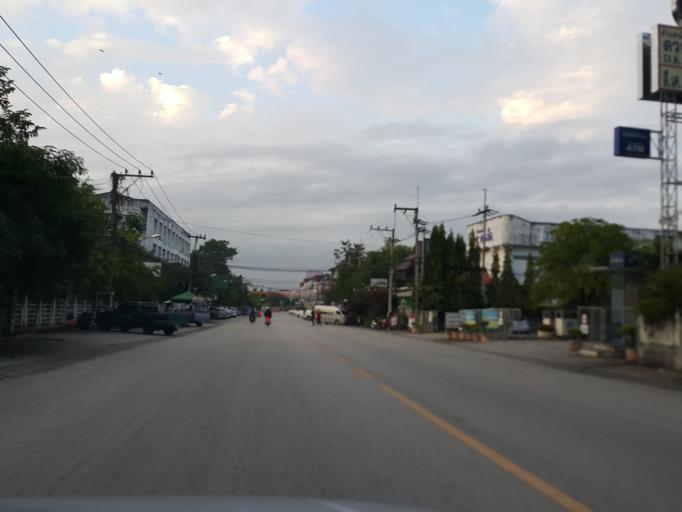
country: TH
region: Lampang
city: Lampang
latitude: 18.2848
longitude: 99.5047
